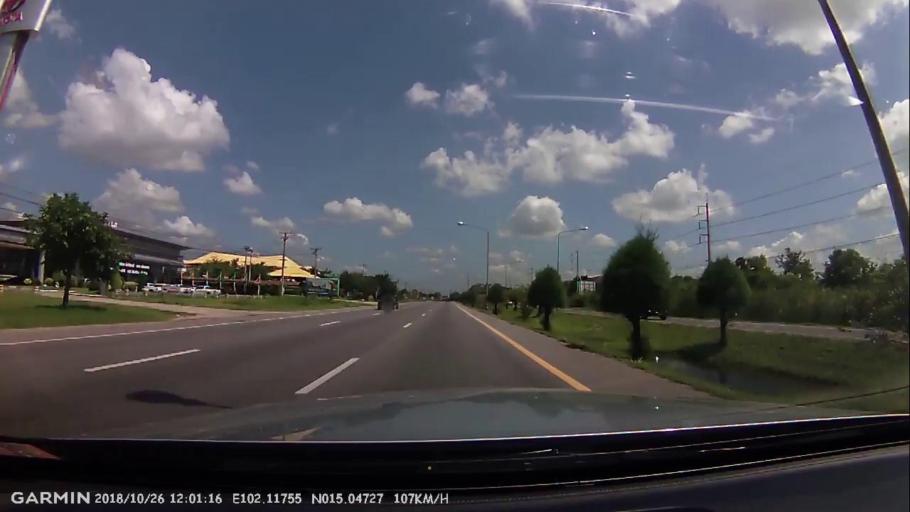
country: TH
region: Nakhon Ratchasima
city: Nakhon Ratchasima
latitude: 15.0473
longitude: 102.1176
